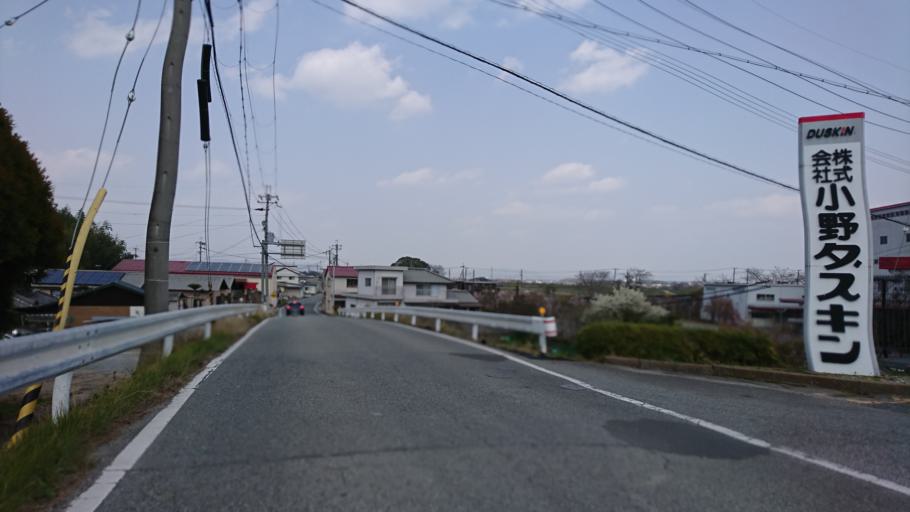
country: JP
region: Hyogo
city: Ono
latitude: 34.8522
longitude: 134.9103
